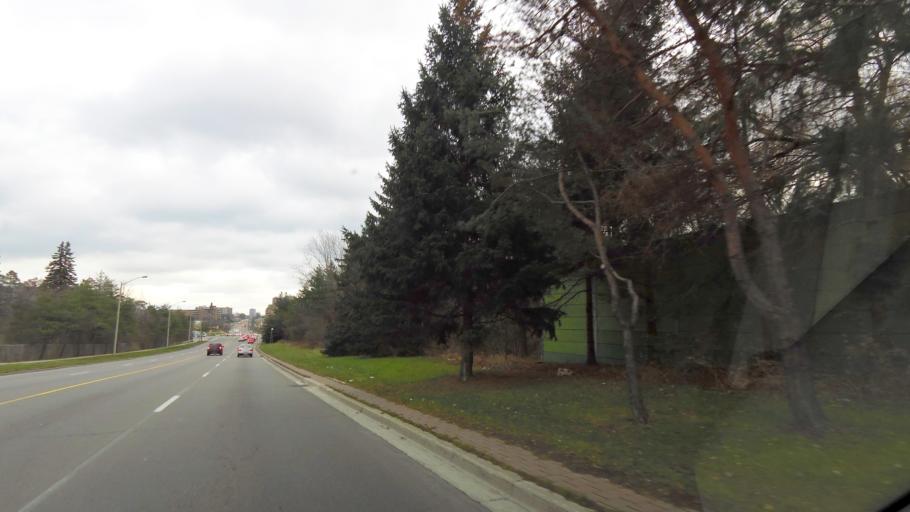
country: CA
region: Ontario
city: Etobicoke
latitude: 43.7453
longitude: -79.5720
